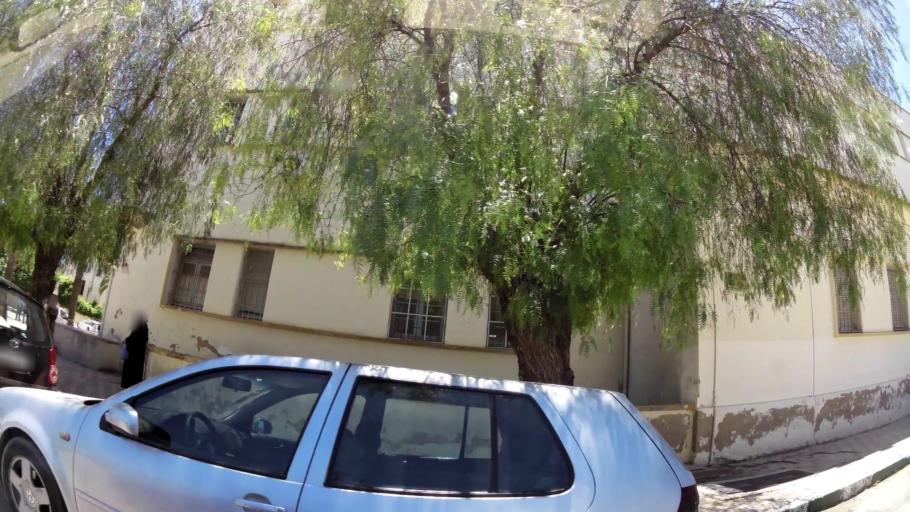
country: MA
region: Meknes-Tafilalet
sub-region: Meknes
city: Meknes
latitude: 33.9032
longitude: -5.5521
